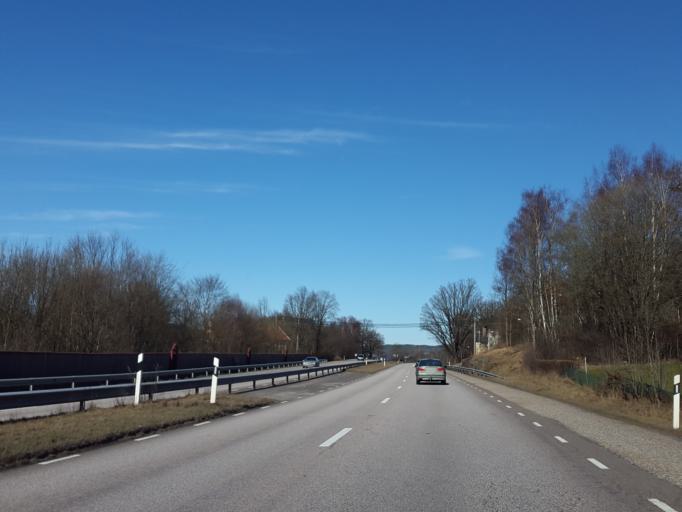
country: SE
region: Vaestra Goetaland
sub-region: Alingsas Kommun
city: Ingared
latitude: 57.8196
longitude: 12.4194
